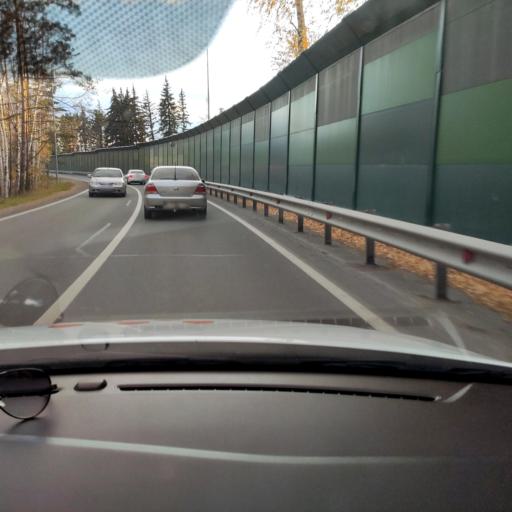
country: RU
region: Tatarstan
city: Verkhniy Uslon
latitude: 55.6291
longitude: 49.0146
